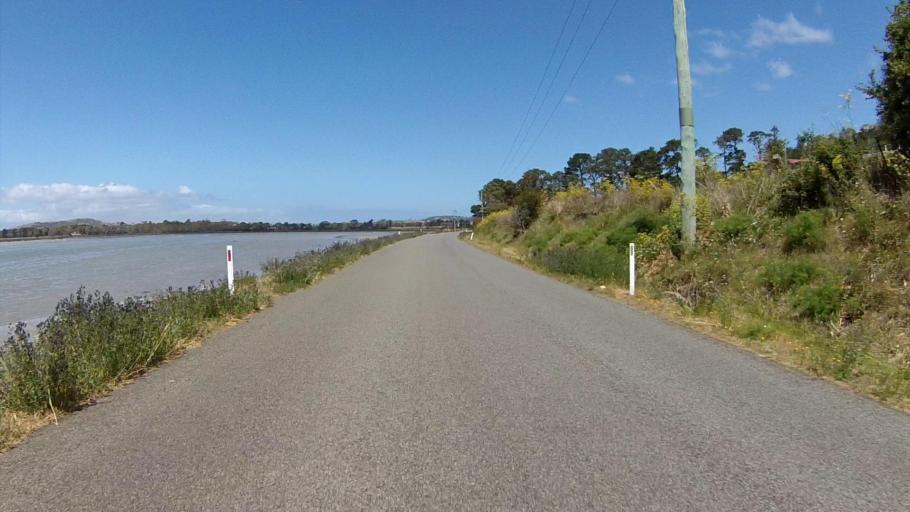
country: AU
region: Tasmania
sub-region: Clarence
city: Lauderdale
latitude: -42.9221
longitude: 147.4806
